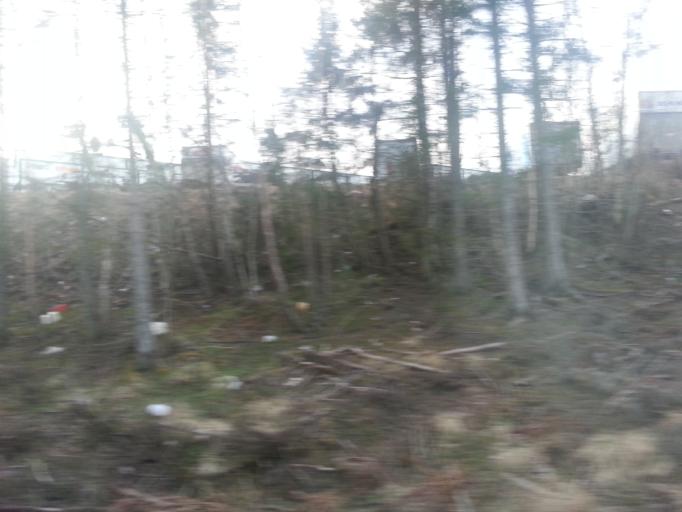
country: NO
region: Sor-Trondelag
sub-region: Trondheim
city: Trondheim
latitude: 63.3455
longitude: 10.3526
